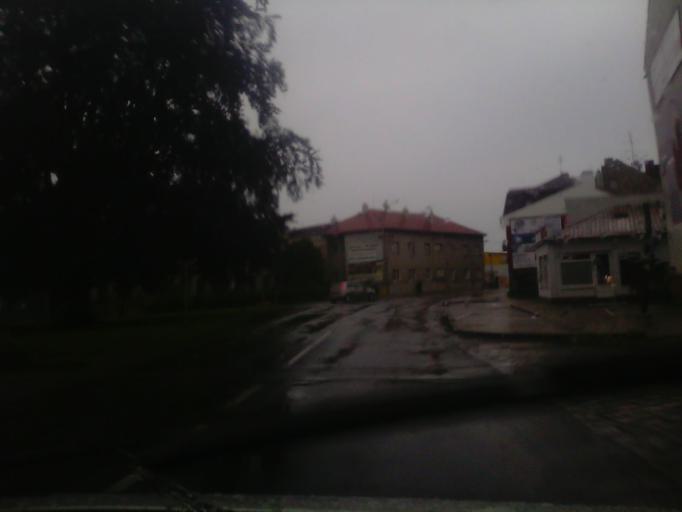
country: CZ
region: Olomoucky
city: Litovel
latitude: 49.6946
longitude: 17.0725
